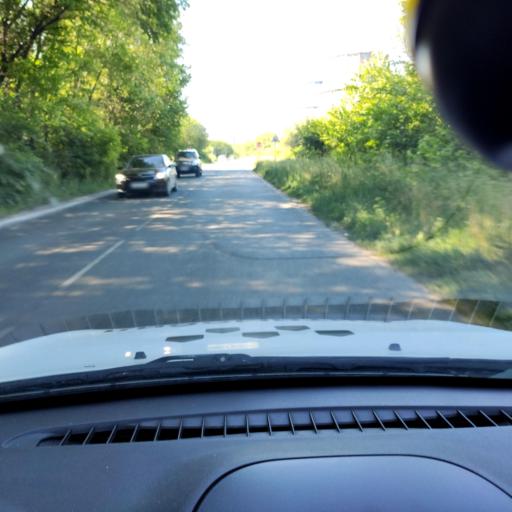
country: RU
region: Samara
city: Tol'yatti
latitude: 53.5797
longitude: 49.2558
